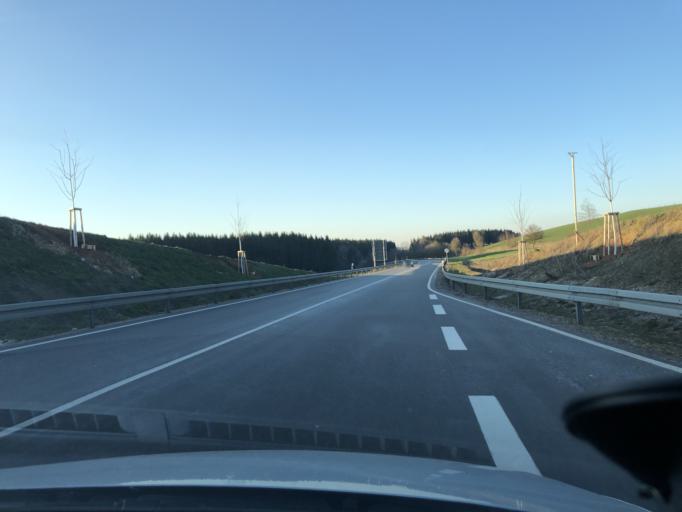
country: DE
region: Baden-Wuerttemberg
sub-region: Freiburg Region
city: Hufingen
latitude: 47.8976
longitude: 8.5090
